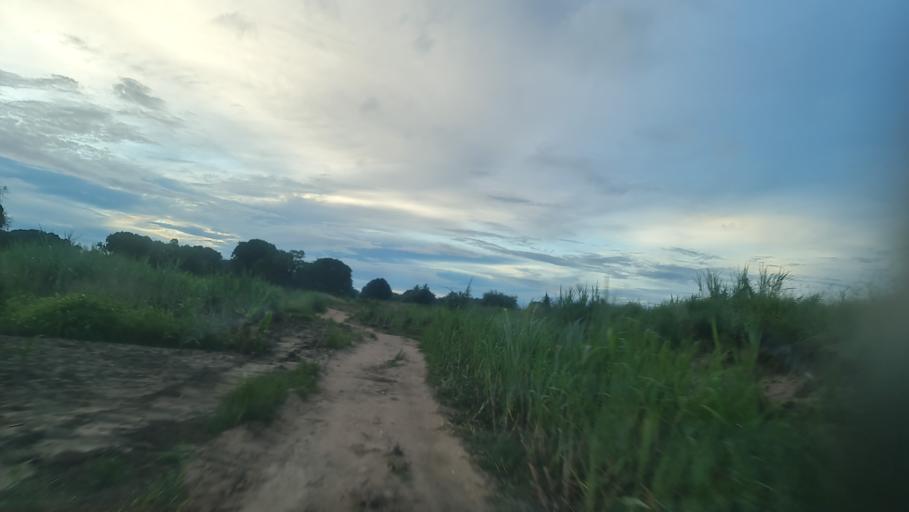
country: MZ
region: Nampula
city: Nampula
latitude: -14.7386
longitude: 39.9302
